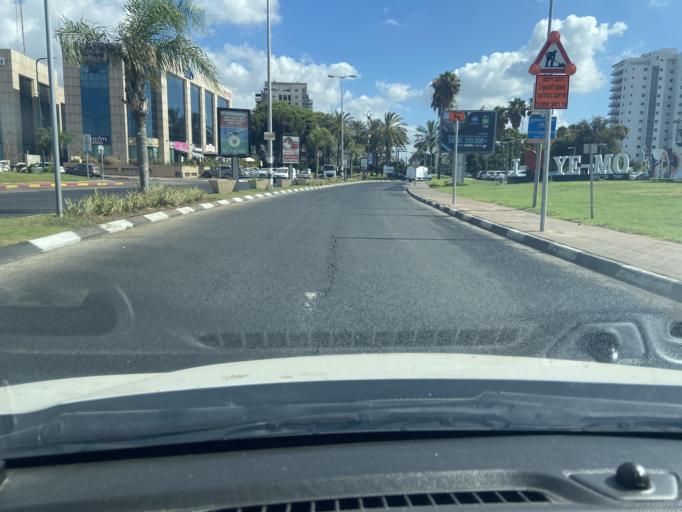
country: IL
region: Central District
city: Yehud
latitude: 32.0269
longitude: 34.8914
